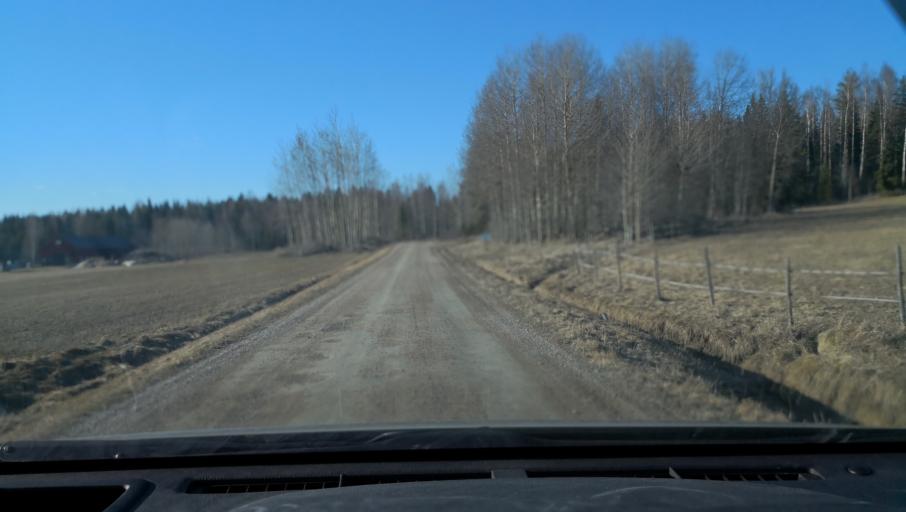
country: SE
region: Vaestmanland
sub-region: Sala Kommun
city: Sala
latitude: 60.1540
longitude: 16.6329
